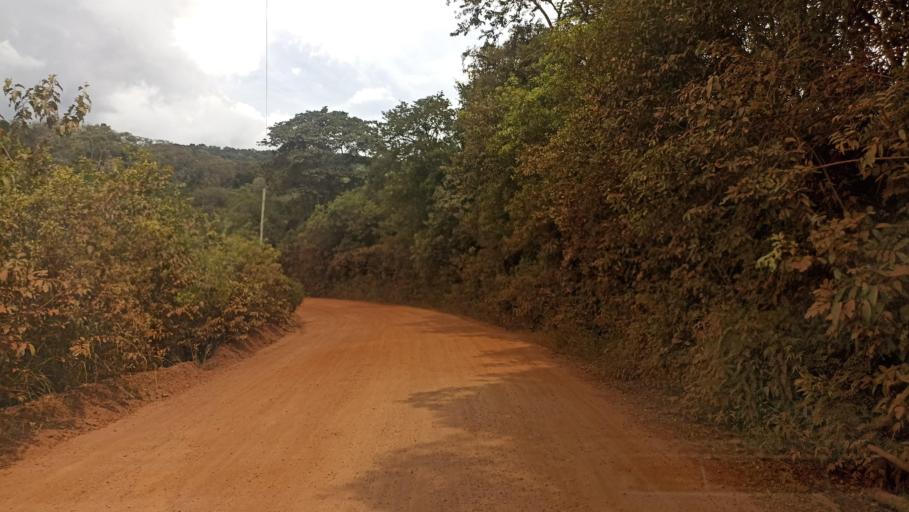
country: BR
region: Minas Gerais
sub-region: Itabirito
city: Itabirito
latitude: -20.3554
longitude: -43.7704
